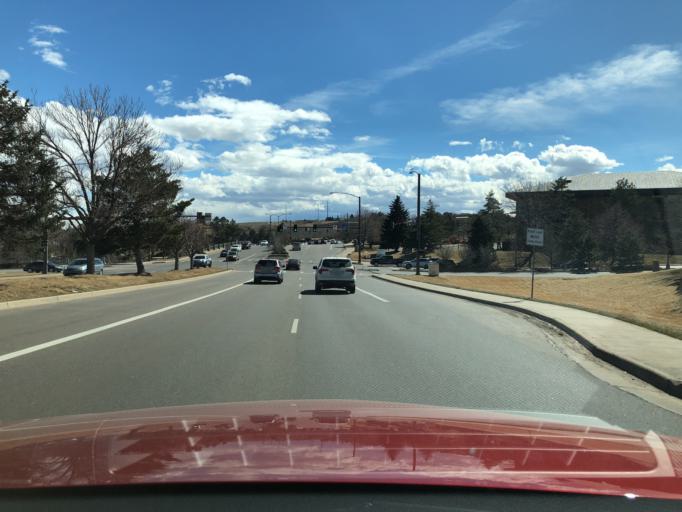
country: US
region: Colorado
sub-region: Jefferson County
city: Applewood
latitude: 39.7392
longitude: -105.1585
